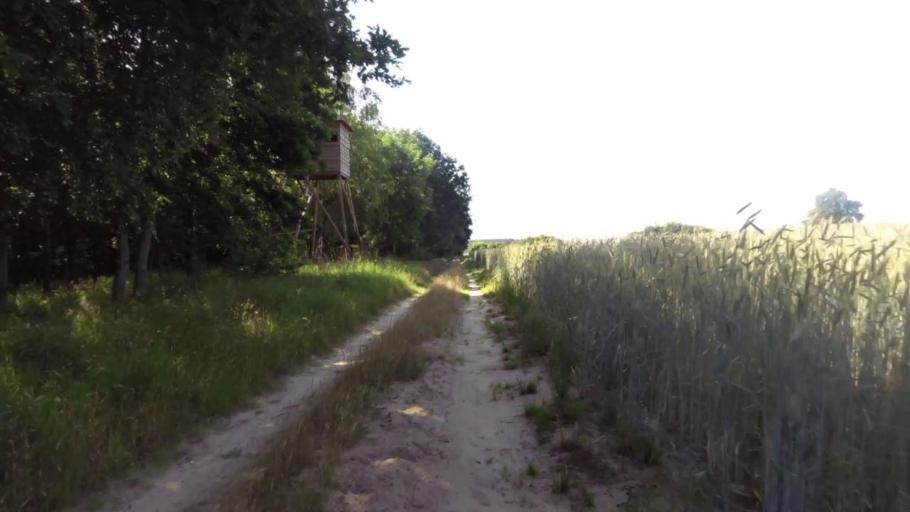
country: PL
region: West Pomeranian Voivodeship
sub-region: Powiat swidwinski
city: Polczyn-Zdroj
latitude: 53.8915
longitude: 16.0897
